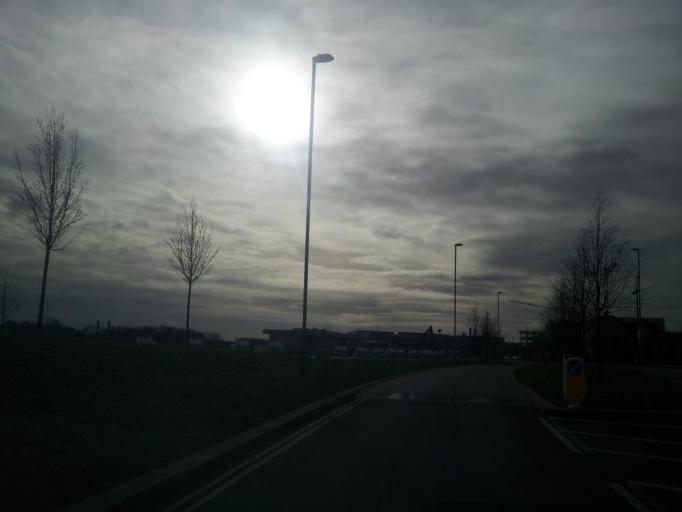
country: GB
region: England
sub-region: Cambridgeshire
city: Girton
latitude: 52.2225
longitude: 0.0912
